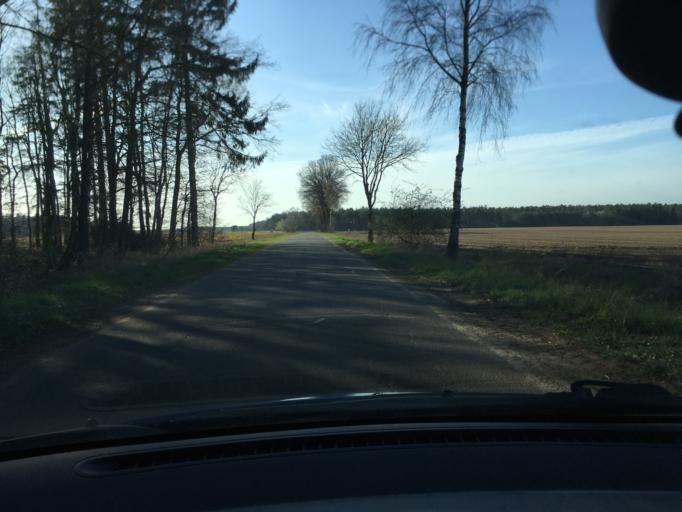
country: DE
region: Lower Saxony
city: Bispingen
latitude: 53.1097
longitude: 10.0219
